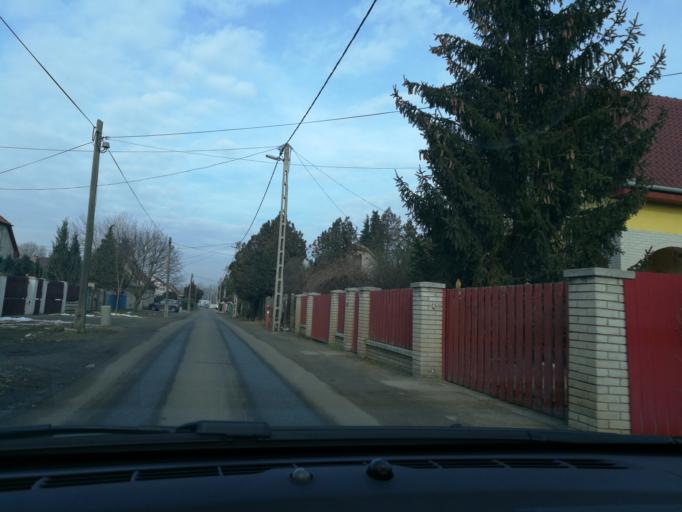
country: HU
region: Szabolcs-Szatmar-Bereg
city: Nyiregyhaza
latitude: 47.9411
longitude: 21.7372
